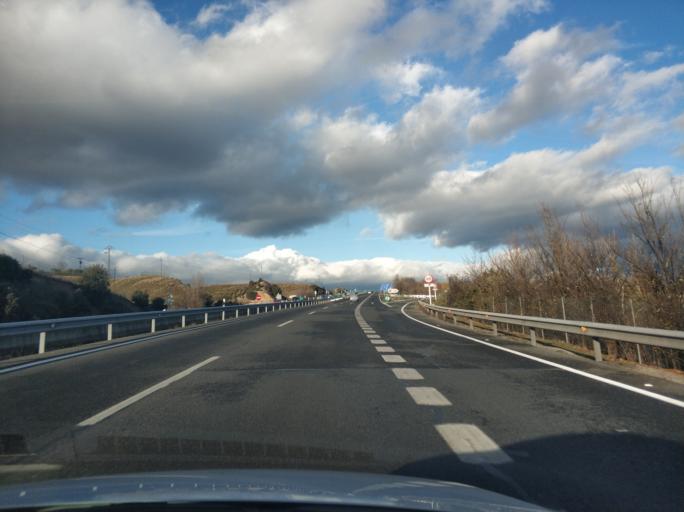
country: ES
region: Madrid
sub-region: Provincia de Madrid
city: El Molar
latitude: 40.7026
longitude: -3.5851
